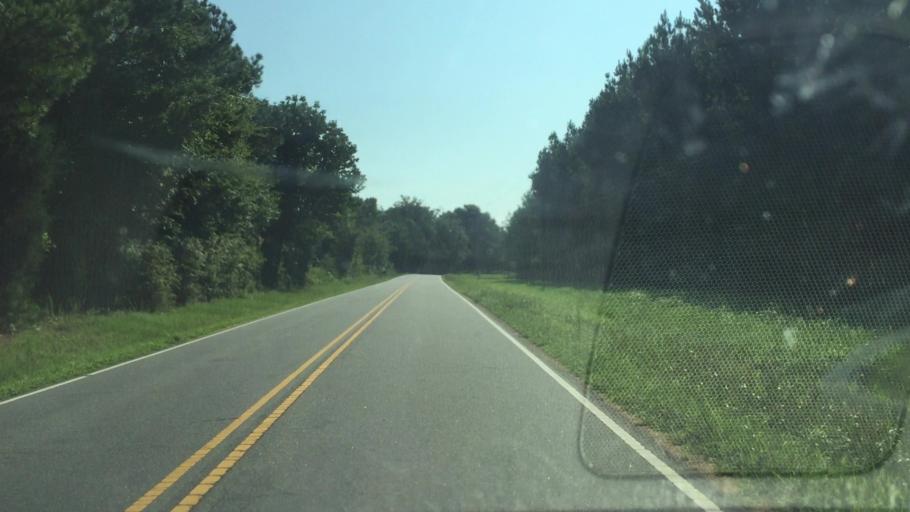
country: US
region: North Carolina
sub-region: Rowan County
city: Enochville
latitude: 35.4867
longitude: -80.7454
